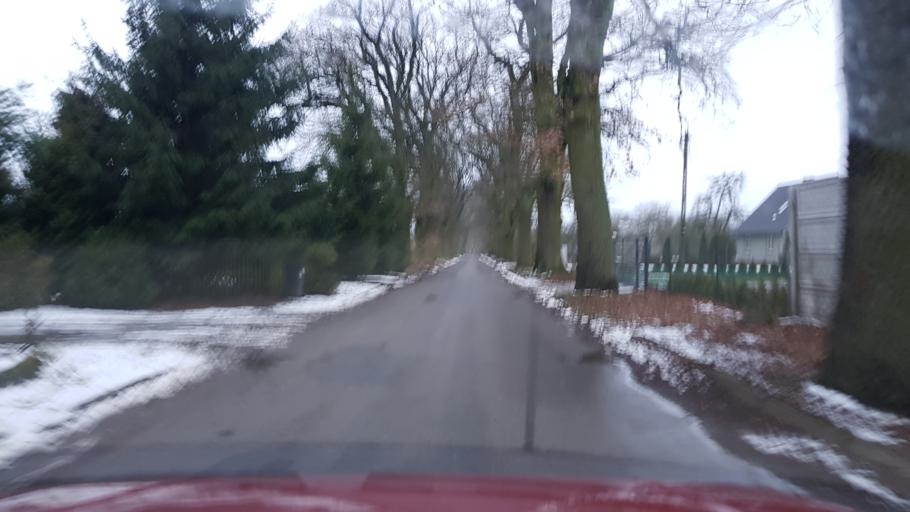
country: PL
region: West Pomeranian Voivodeship
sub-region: Powiat goleniowski
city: Mosty
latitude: 53.5018
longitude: 14.9204
